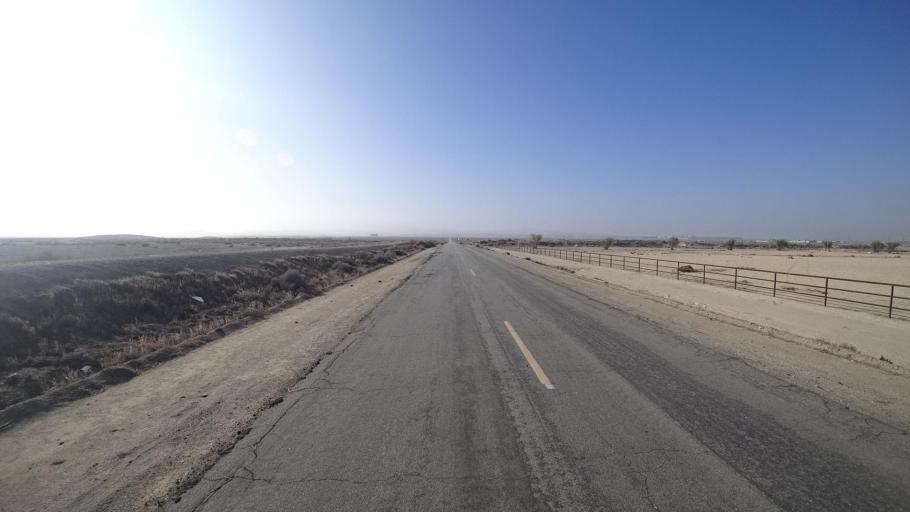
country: US
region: California
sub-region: Kern County
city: Maricopa
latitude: 35.1011
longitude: -119.3748
